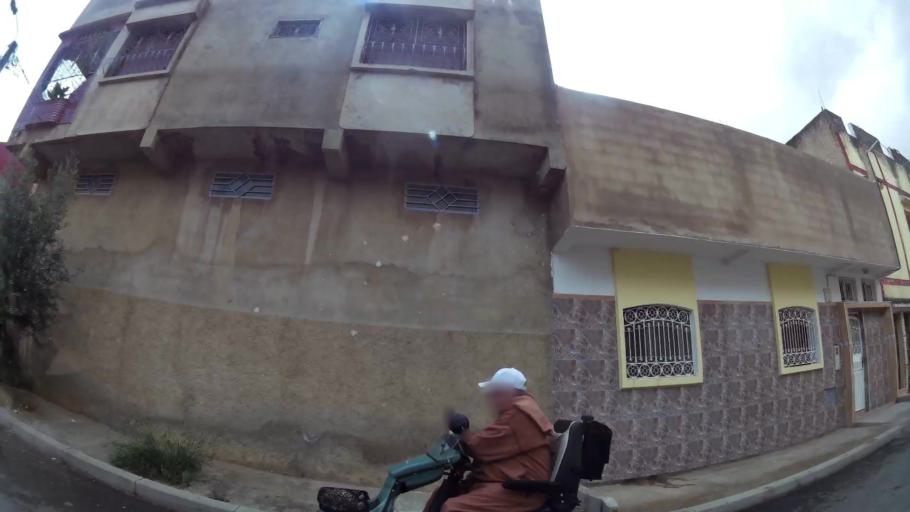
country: MA
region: Rabat-Sale-Zemmour-Zaer
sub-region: Khemisset
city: Tiflet
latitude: 33.8917
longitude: -6.3330
